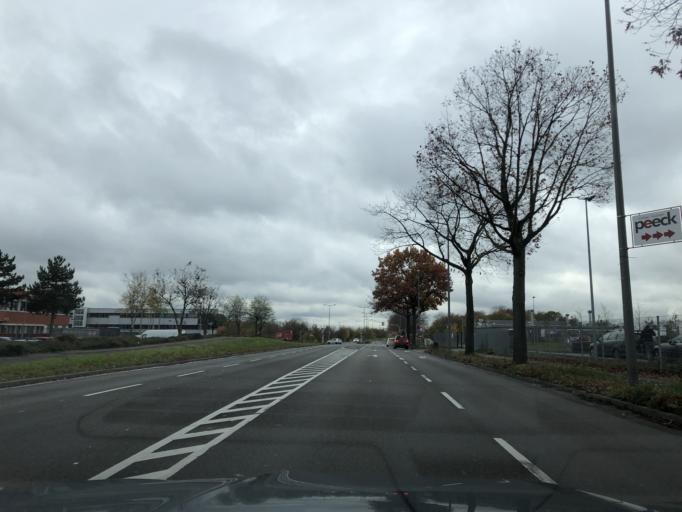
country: DE
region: Hesse
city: Viernheim
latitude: 49.5129
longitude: 8.5566
